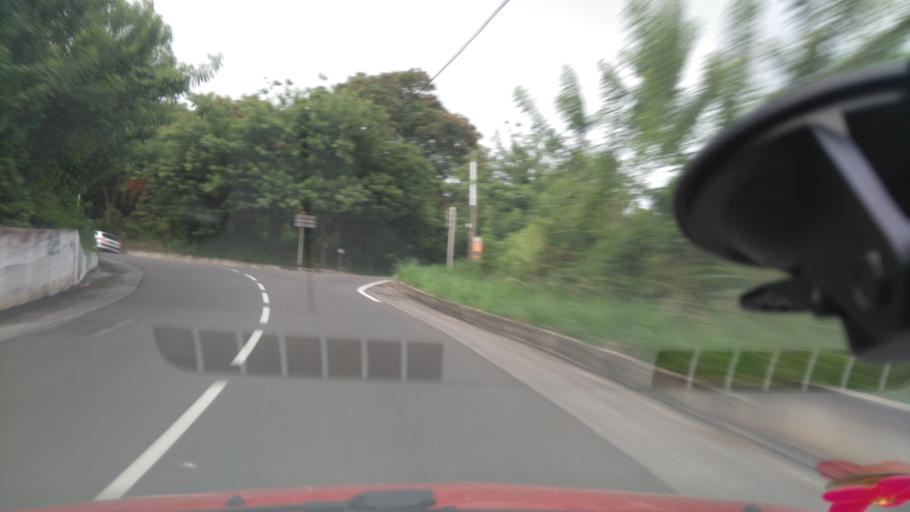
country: MQ
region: Martinique
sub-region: Martinique
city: Ducos
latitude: 14.5529
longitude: -60.9609
